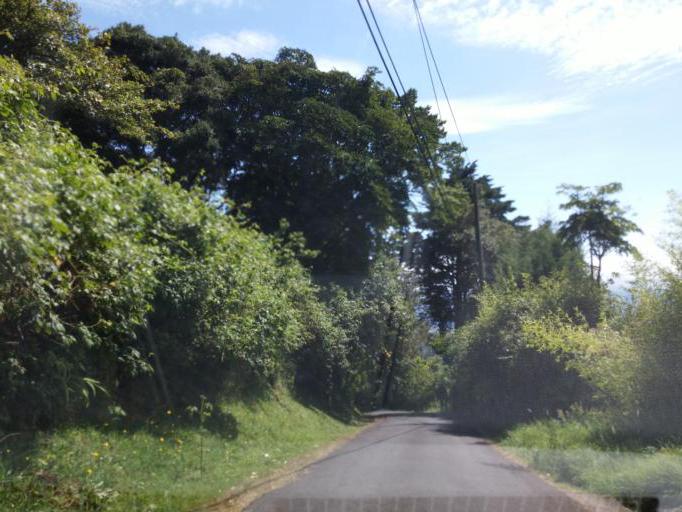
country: CR
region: Heredia
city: Santo Domingo
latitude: 10.1061
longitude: -84.1203
